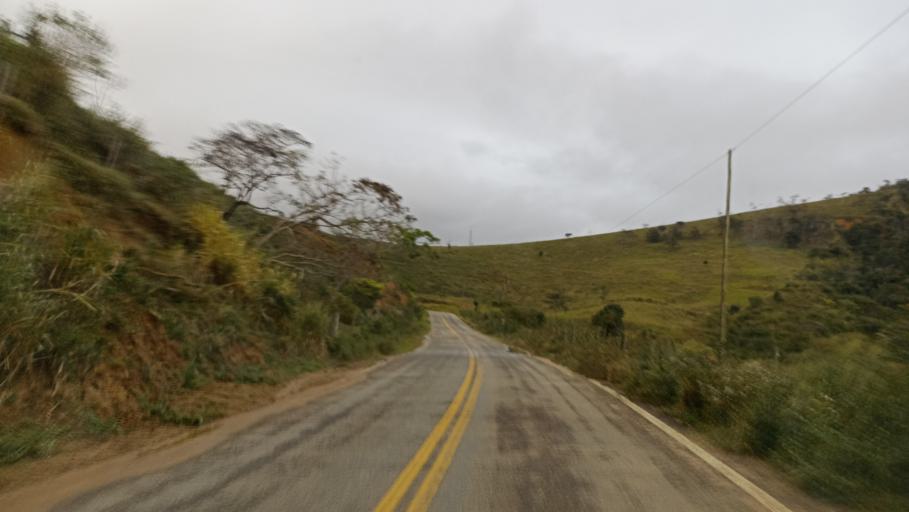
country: BR
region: Minas Gerais
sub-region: Joaima
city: Joaima
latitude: -16.6721
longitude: -40.5300
